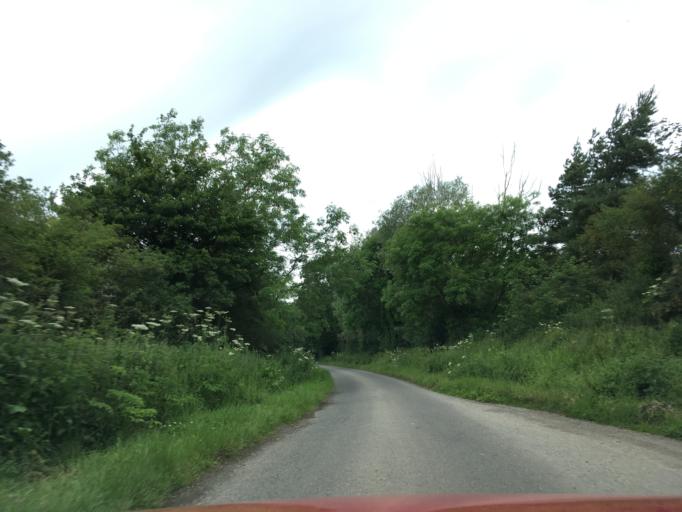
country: GB
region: England
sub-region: Gloucestershire
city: Tetbury
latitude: 51.6026
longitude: -2.1651
